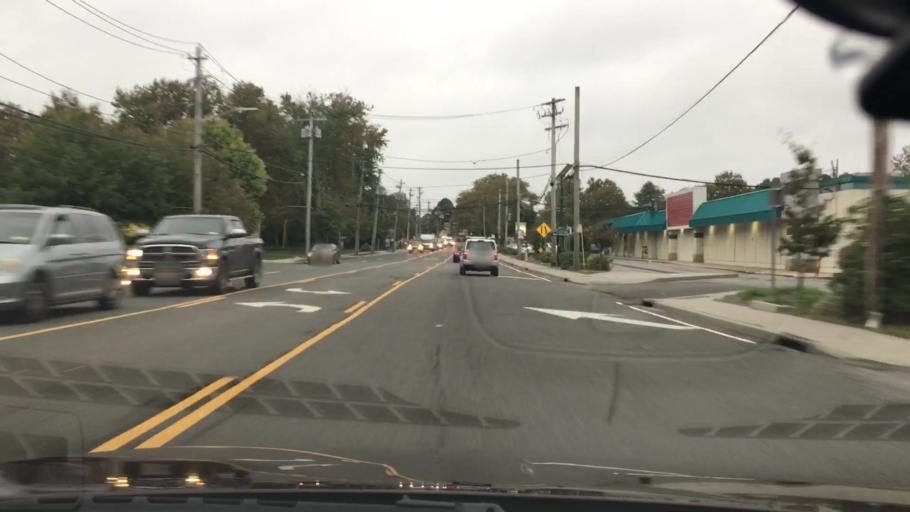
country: US
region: New York
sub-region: Suffolk County
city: Hauppauge
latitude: 40.8290
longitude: -73.1994
